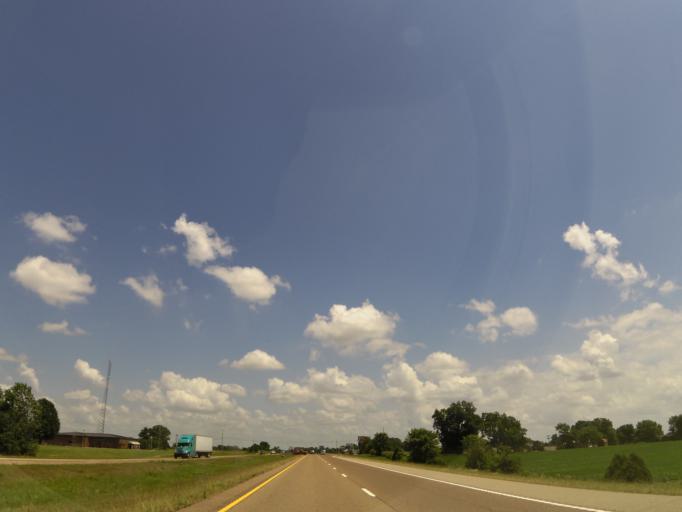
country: US
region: Tennessee
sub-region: Crockett County
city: Alamo
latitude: 35.7845
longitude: -89.1464
